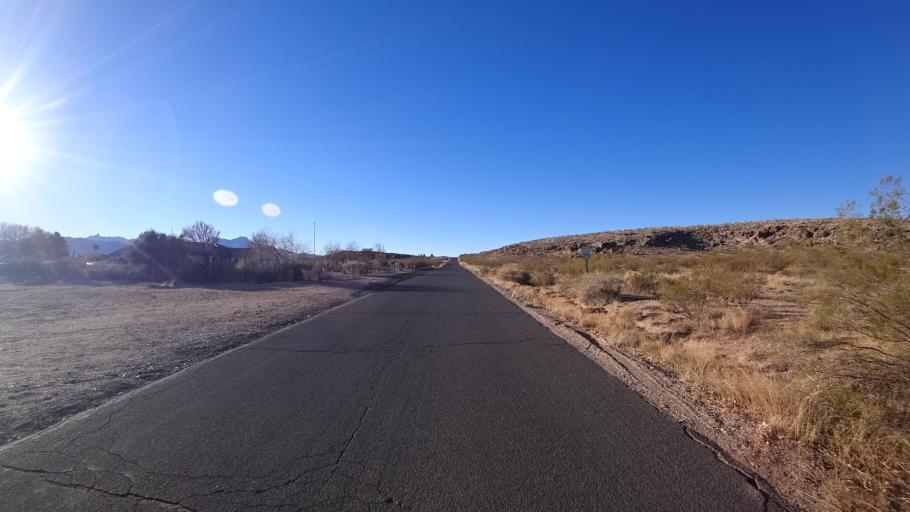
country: US
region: Arizona
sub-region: Mohave County
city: Kingman
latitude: 35.2090
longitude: -114.0026
